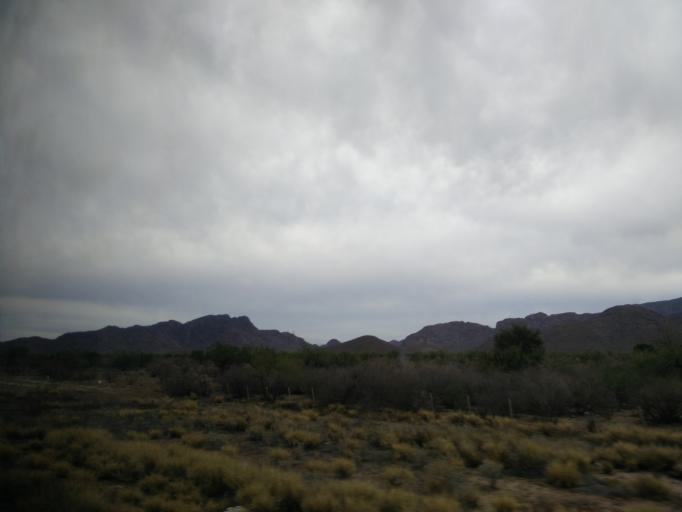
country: MX
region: Sonora
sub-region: Hermosillo
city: Miguel Aleman (La Doce)
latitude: 28.5667
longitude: -111.0332
